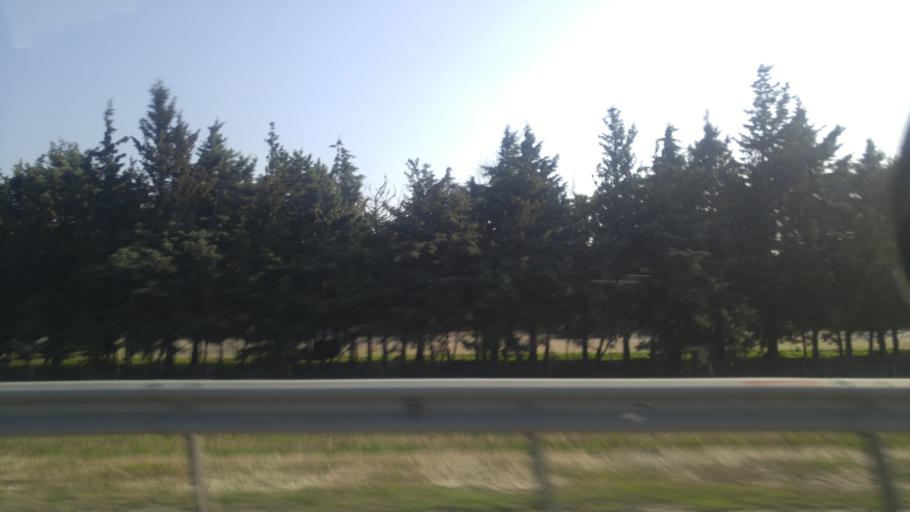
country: TR
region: Istanbul
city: Chekmejeh
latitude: 41.0094
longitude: 28.5248
